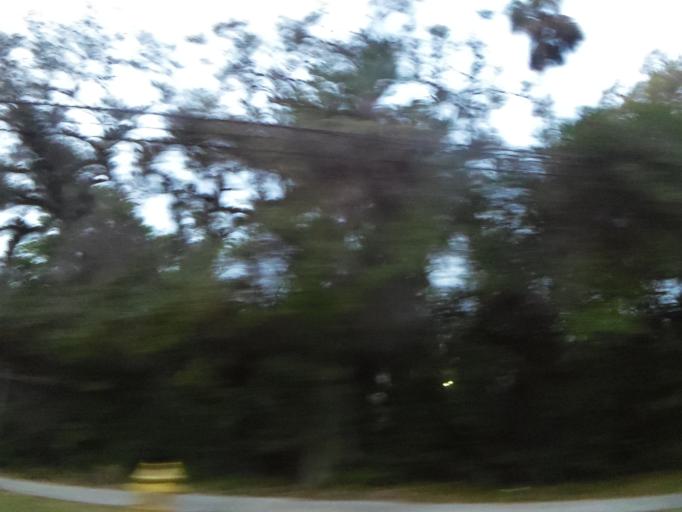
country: US
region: Florida
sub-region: Duval County
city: Atlantic Beach
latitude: 30.3715
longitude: -81.4089
